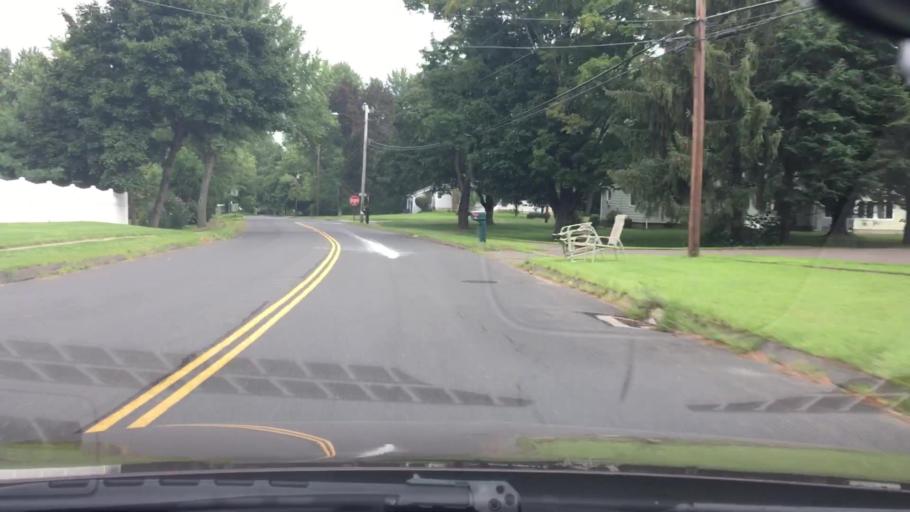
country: US
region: Connecticut
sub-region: Tolland County
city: Rockville
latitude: 41.8295
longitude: -72.4902
